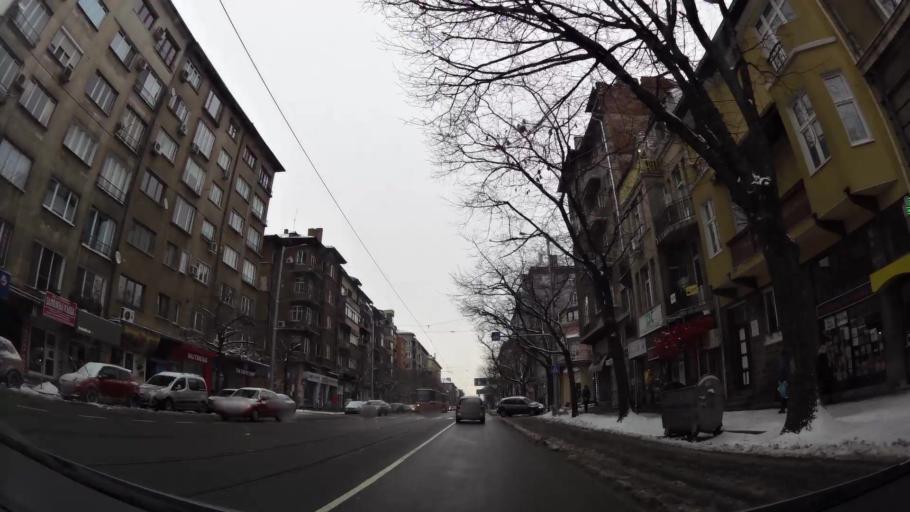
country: BG
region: Sofia-Capital
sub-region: Stolichna Obshtina
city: Sofia
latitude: 42.6985
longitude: 23.3318
